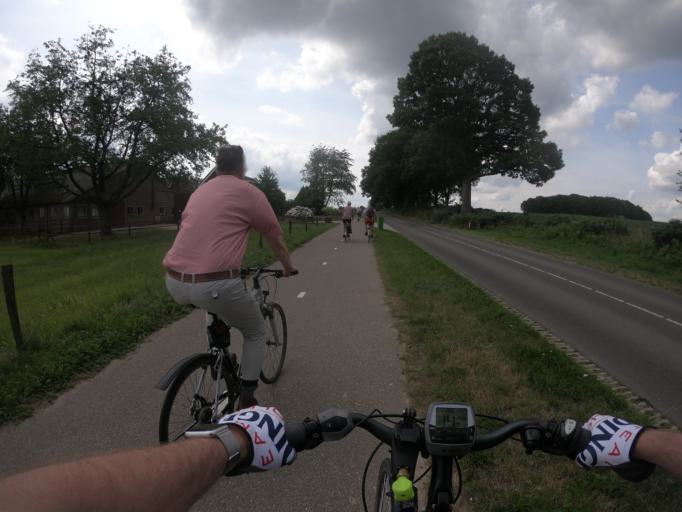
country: NL
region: Gelderland
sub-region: Gemeente Groesbeek
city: Groesbeek
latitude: 51.7932
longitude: 5.9481
